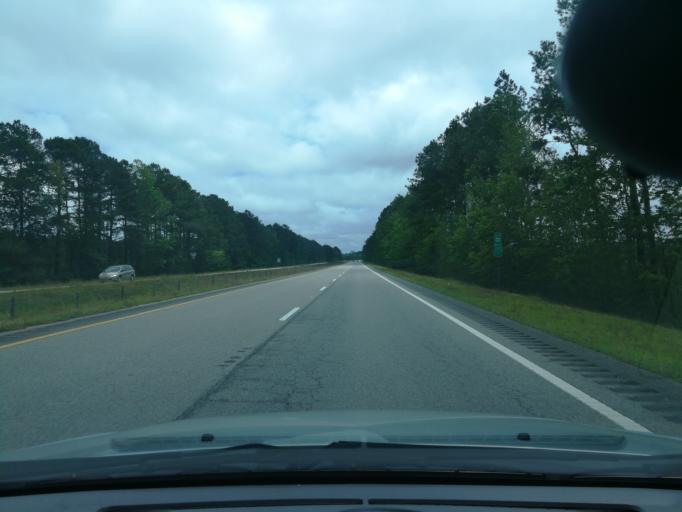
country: US
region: North Carolina
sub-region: Chowan County
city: Edenton
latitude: 35.9066
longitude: -76.4699
